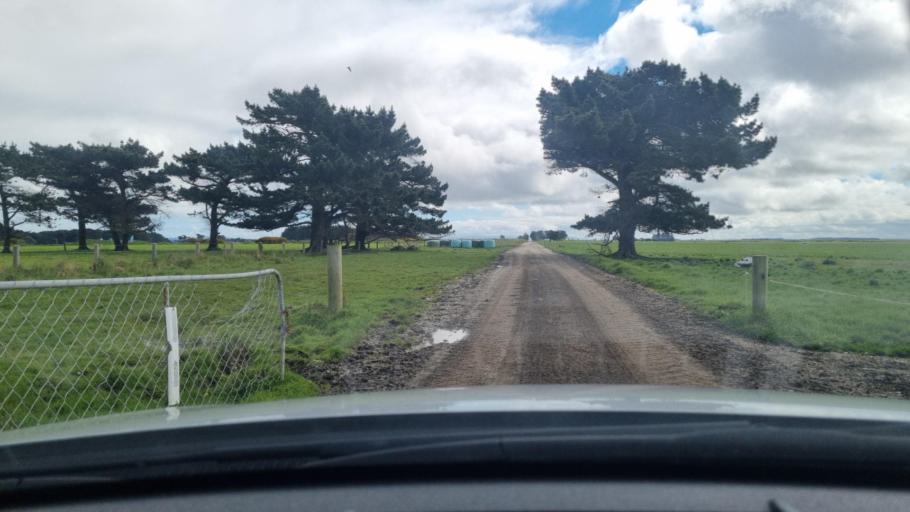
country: NZ
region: Southland
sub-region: Invercargill City
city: Bluff
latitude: -46.5654
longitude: 168.4999
